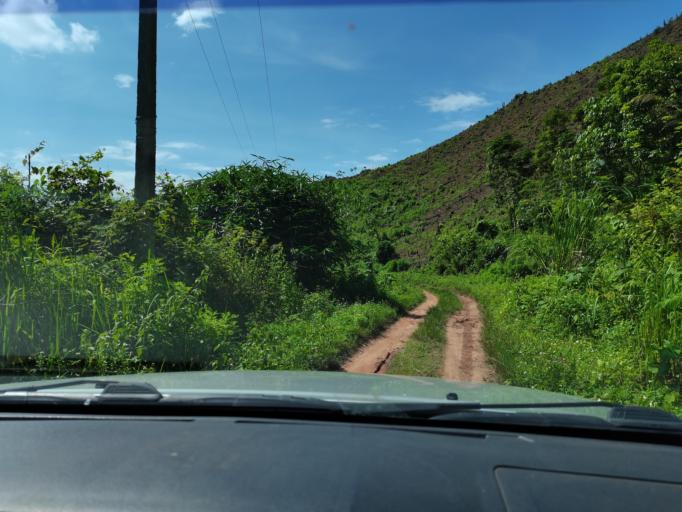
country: LA
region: Loungnamtha
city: Muang Nale
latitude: 20.5547
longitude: 101.0653
